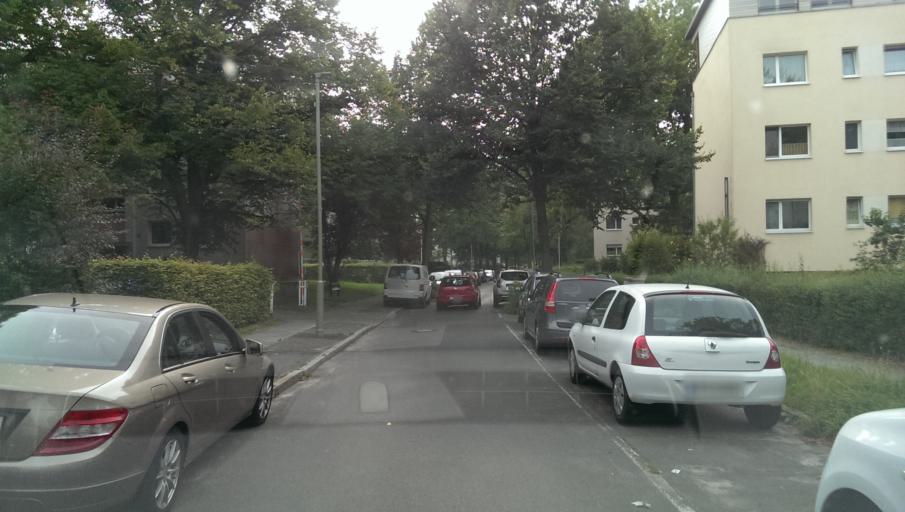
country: DE
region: Brandenburg
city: Teltow
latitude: 52.4100
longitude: 13.2546
